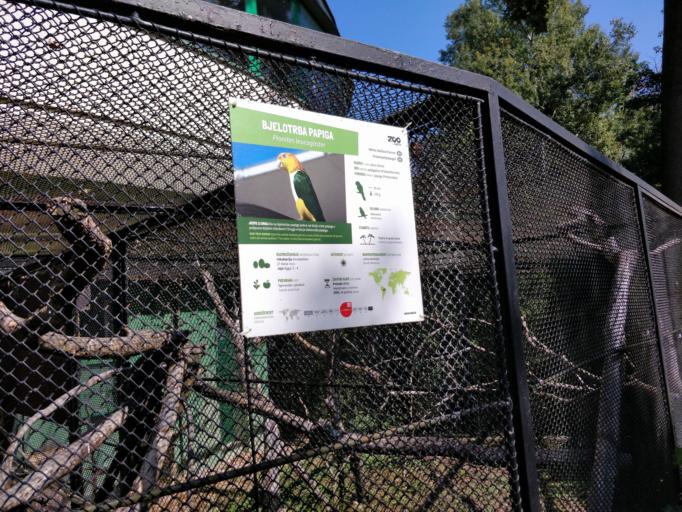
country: HR
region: Grad Zagreb
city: Zagreb
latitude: 45.8209
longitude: 16.0195
